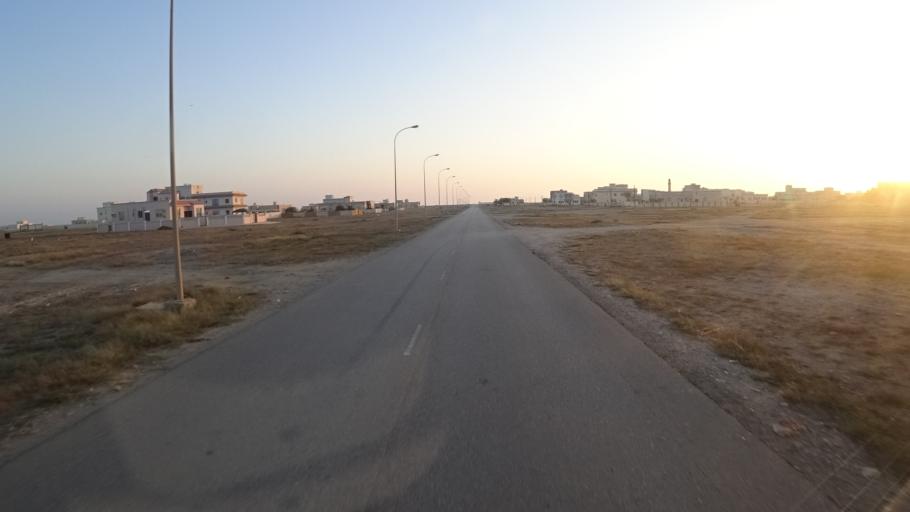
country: OM
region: Zufar
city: Salalah
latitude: 16.9845
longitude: 54.7125
